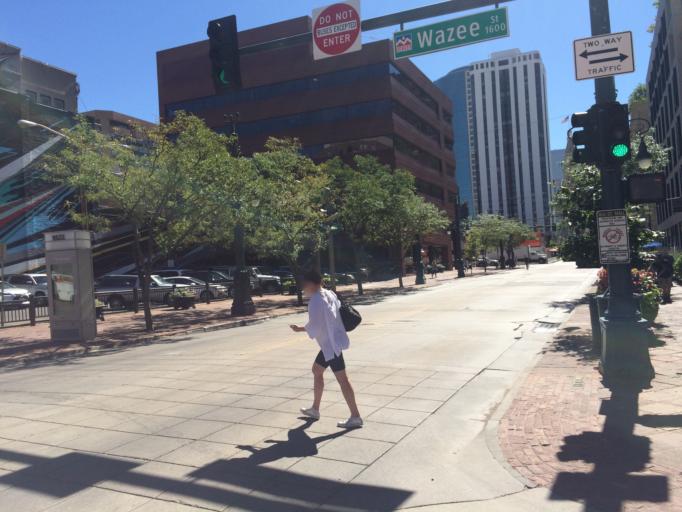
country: US
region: Colorado
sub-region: Denver County
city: Denver
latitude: 39.7511
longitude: -105.0001
